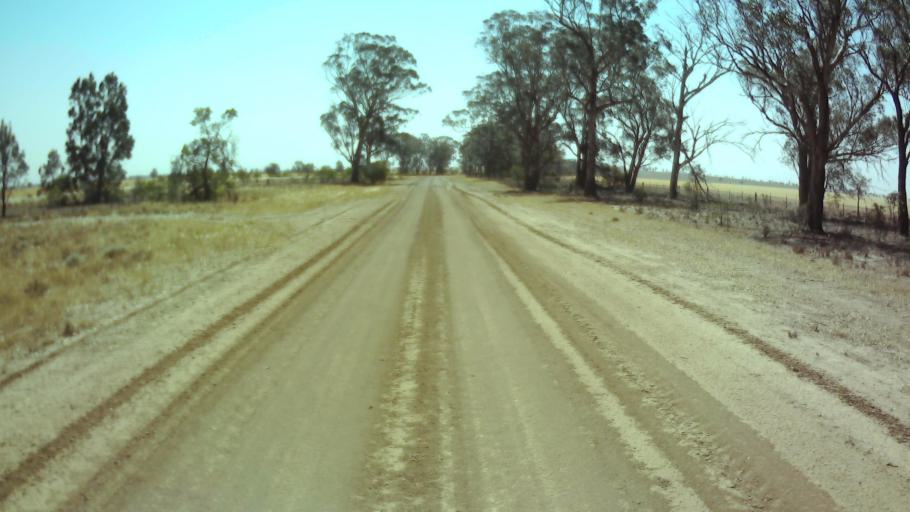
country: AU
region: New South Wales
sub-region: Weddin
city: Grenfell
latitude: -33.9222
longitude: 147.7820
